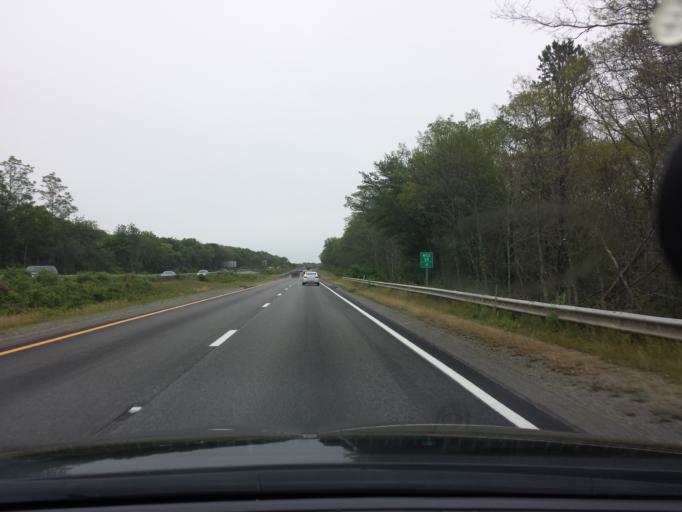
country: US
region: Massachusetts
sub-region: Barnstable County
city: Sandwich
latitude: 41.7380
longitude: -70.4805
